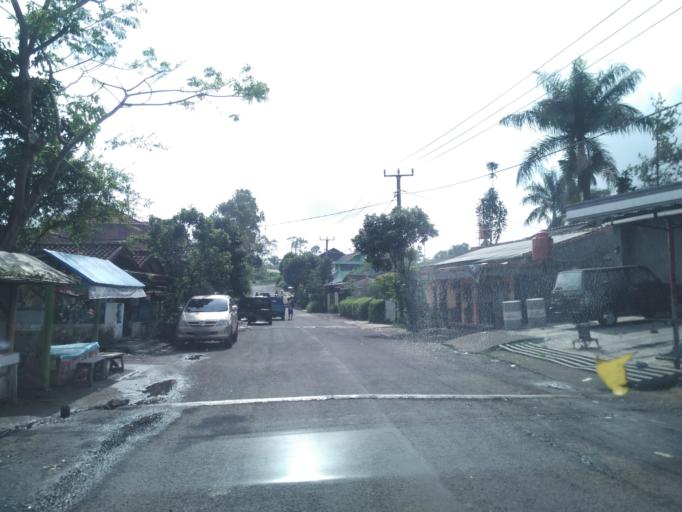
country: ID
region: West Java
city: Ciranjang-hilir
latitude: -6.7479
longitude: 107.0582
